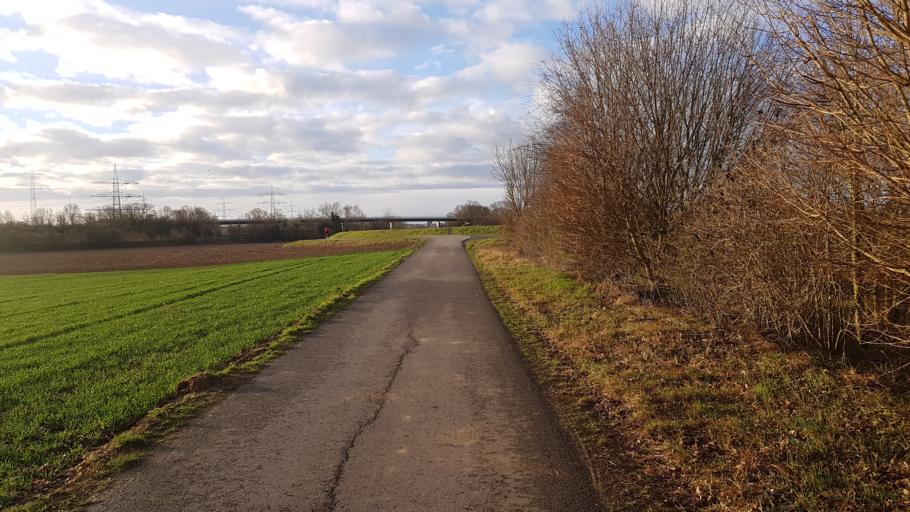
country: DE
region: Baden-Wuerttemberg
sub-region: Karlsruhe Region
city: Walldorf
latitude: 49.3137
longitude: 8.6655
